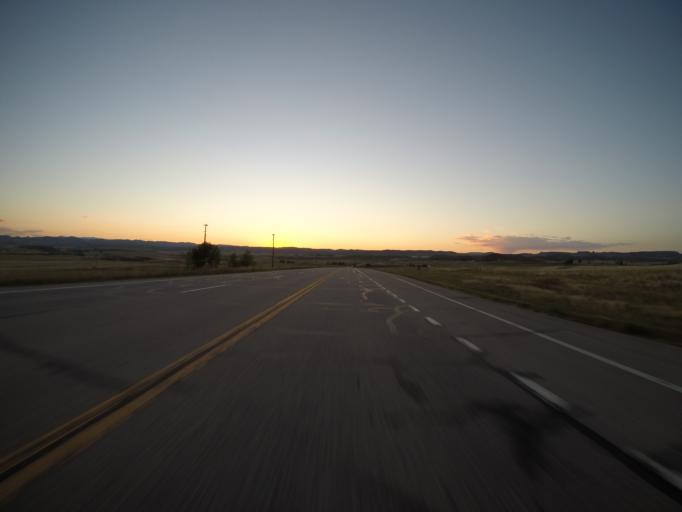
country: US
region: Colorado
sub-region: Larimer County
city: Laporte
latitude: 40.7997
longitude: -105.2273
